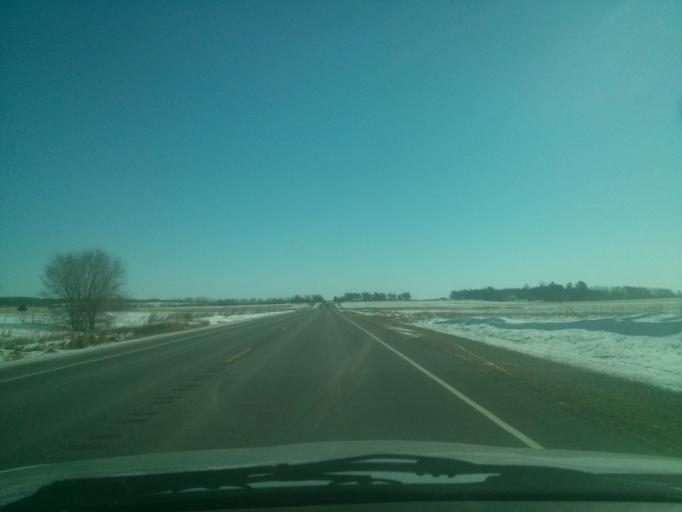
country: US
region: Wisconsin
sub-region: Polk County
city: Clear Lake
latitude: 45.1364
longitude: -92.3621
